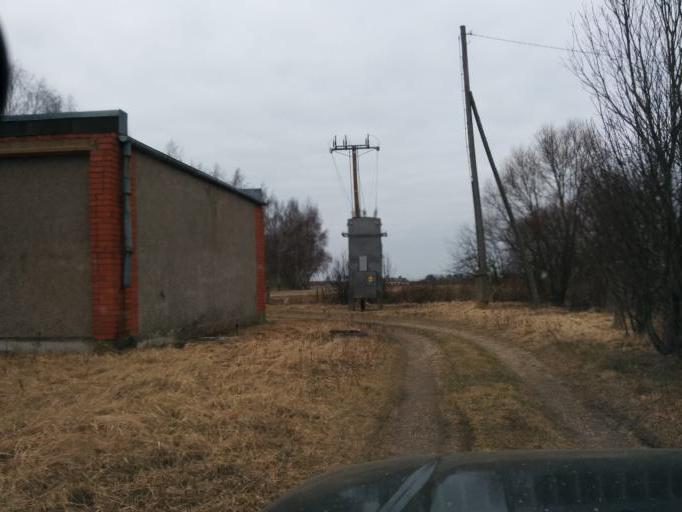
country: LV
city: Tireli
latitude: 56.9111
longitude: 23.6237
